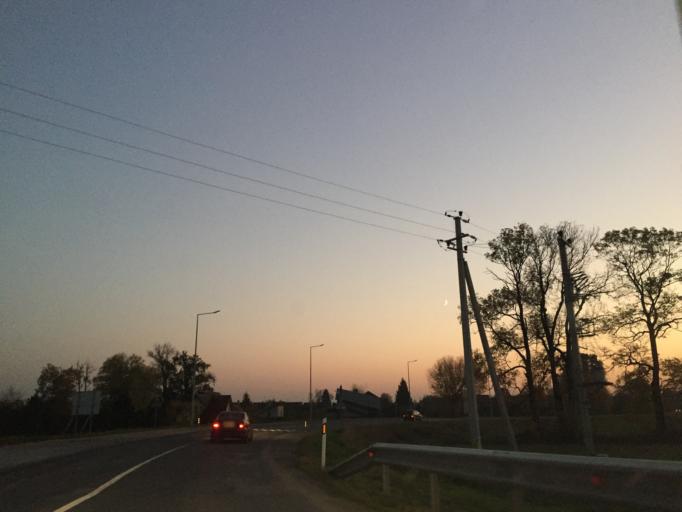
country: LT
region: Klaipedos apskritis
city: Kretinga
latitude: 55.9025
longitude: 21.2438
